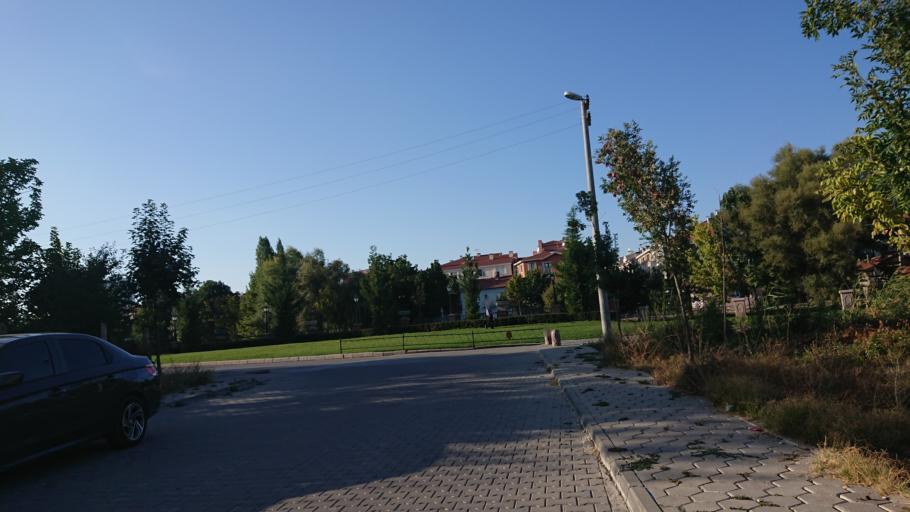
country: TR
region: Eskisehir
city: Eskisehir
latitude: 39.7673
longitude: 30.4925
